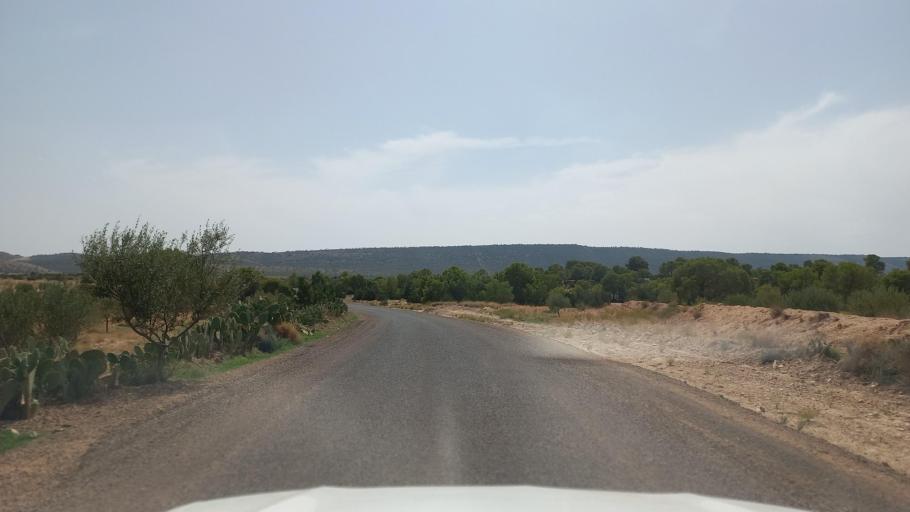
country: TN
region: Al Qasrayn
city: Sbiba
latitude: 35.3951
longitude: 8.9485
